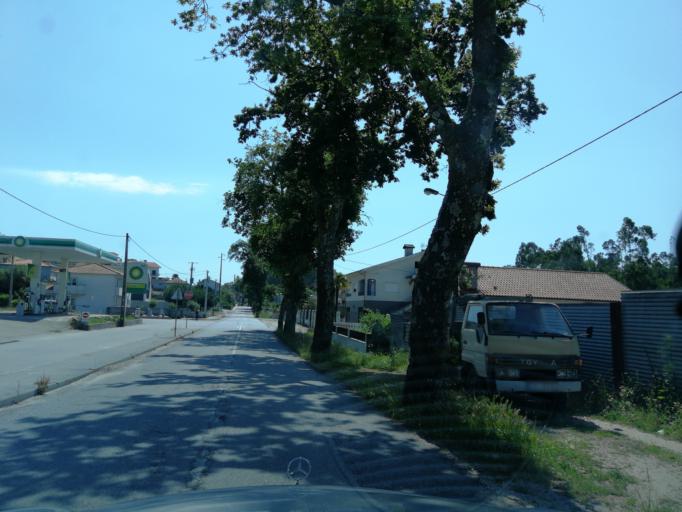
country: PT
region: Braga
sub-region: Braga
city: Adaufe
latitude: 41.5541
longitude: -8.3473
